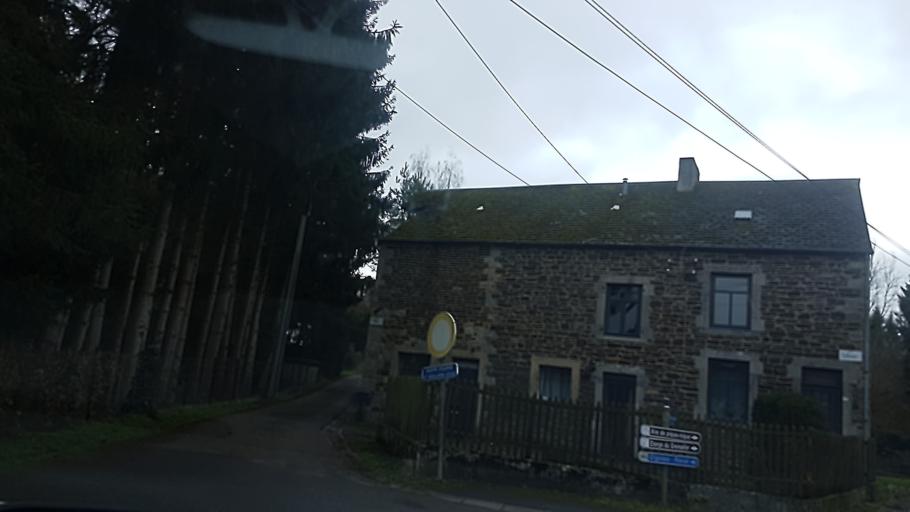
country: BE
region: Wallonia
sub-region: Province de Namur
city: Couvin
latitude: 50.0695
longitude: 4.6064
